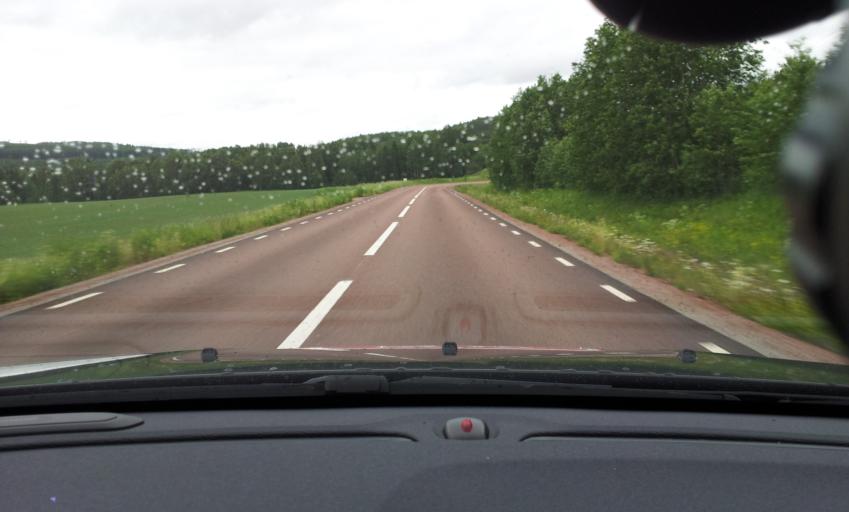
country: SE
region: Jaemtland
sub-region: Ragunda Kommun
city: Hammarstrand
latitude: 63.0573
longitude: 16.4792
